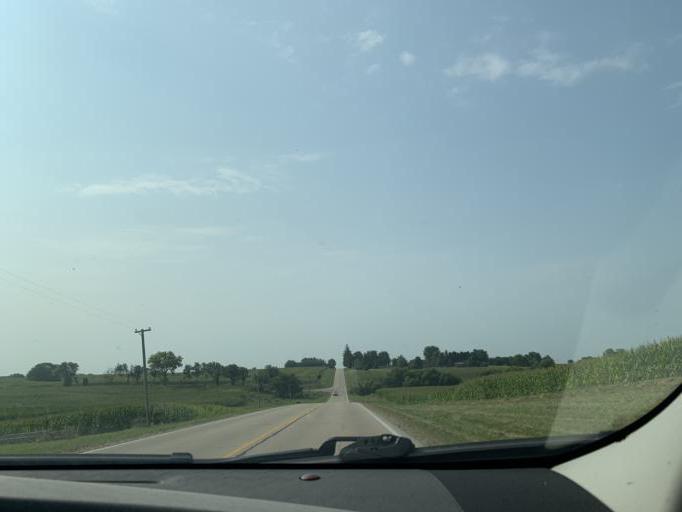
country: US
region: Illinois
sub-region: Carroll County
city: Milledgeville
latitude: 41.8468
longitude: -89.8045
